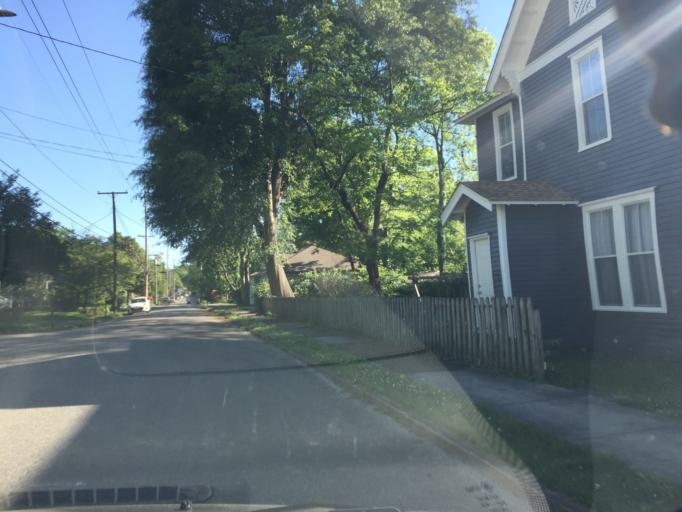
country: US
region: Tennessee
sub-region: Hamilton County
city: Lookout Mountain
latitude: 34.9907
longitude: -85.3296
